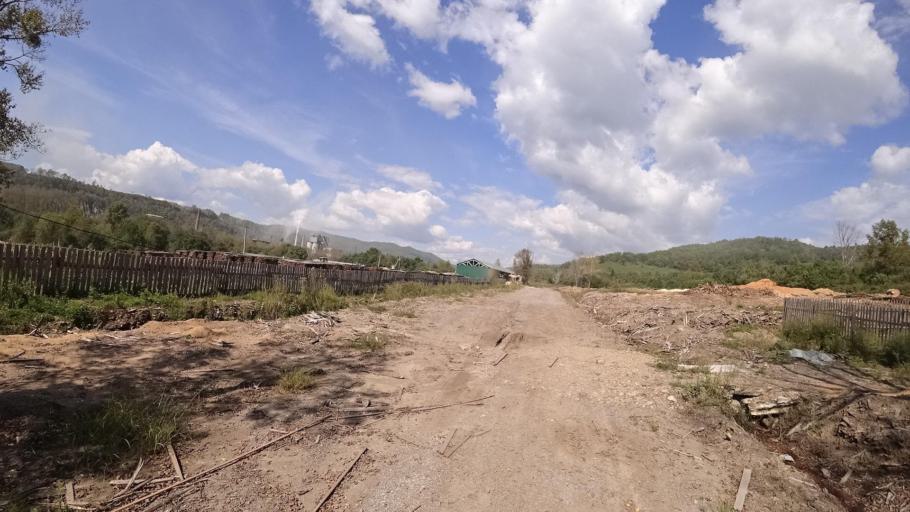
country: RU
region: Jewish Autonomous Oblast
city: Londoko
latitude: 49.0110
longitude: 131.9420
